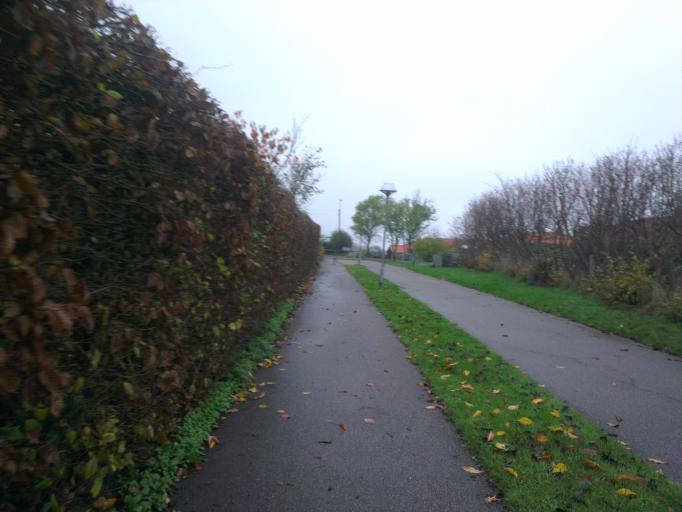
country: DK
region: Capital Region
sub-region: Frederikssund Kommune
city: Jaegerspris
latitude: 55.8512
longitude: 11.9969
